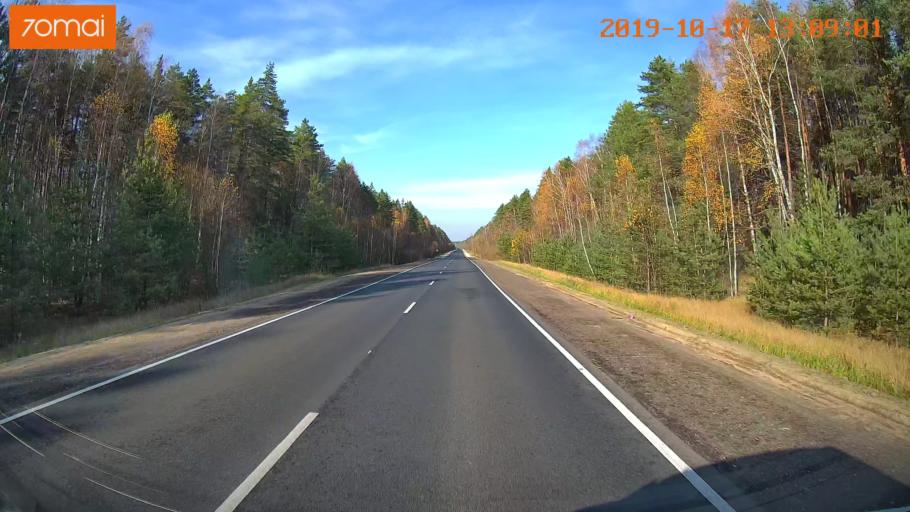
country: RU
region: Rjazan
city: Syntul
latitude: 54.9974
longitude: 41.2657
